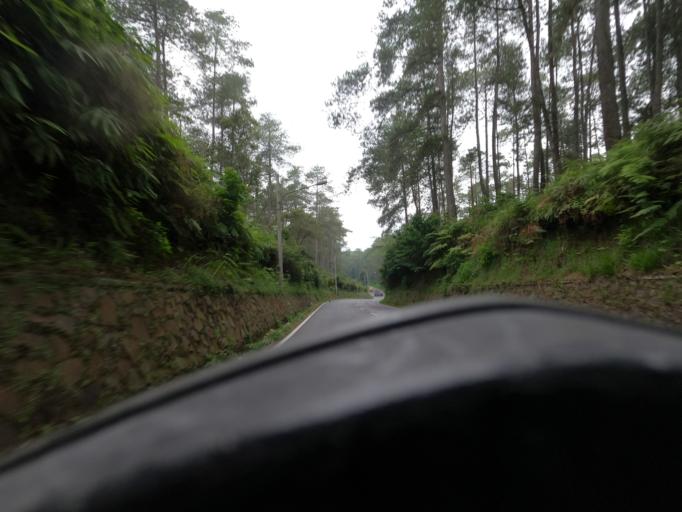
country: ID
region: West Java
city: Lembang
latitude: -6.7760
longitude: 107.6391
